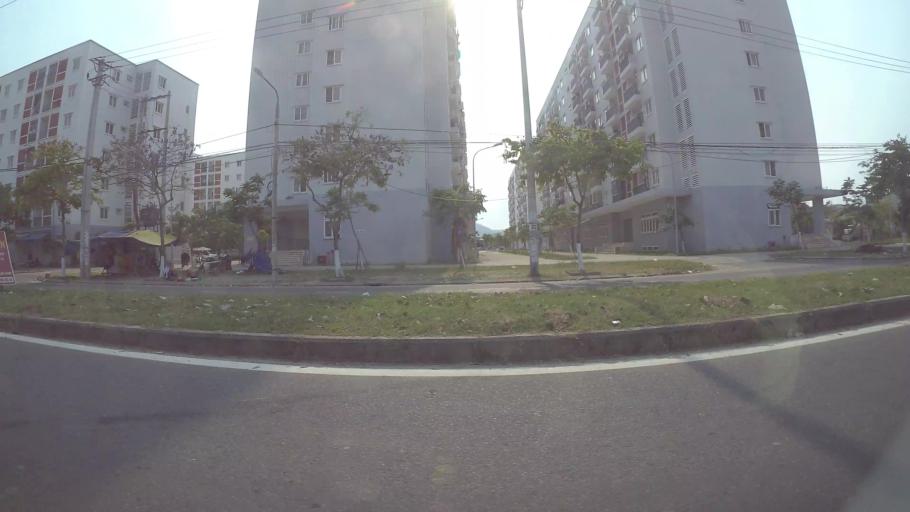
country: VN
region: Da Nang
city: Thanh Khe
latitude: 16.0454
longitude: 108.1758
